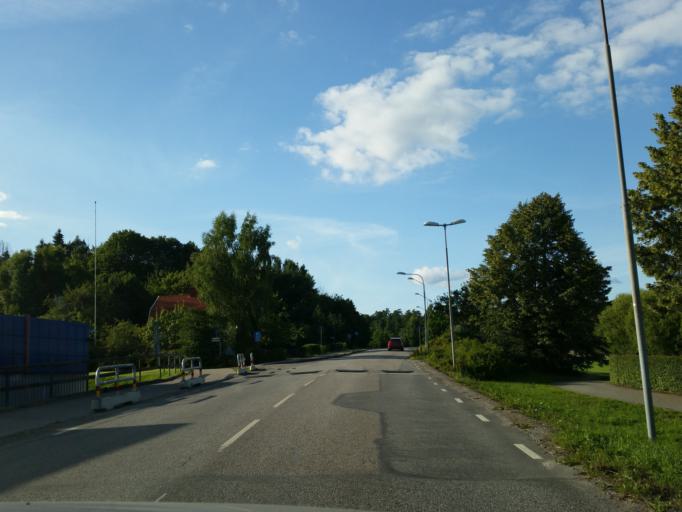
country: SE
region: Soedermanland
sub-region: Trosa Kommun
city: Vagnharad
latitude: 58.9464
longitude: 17.4876
